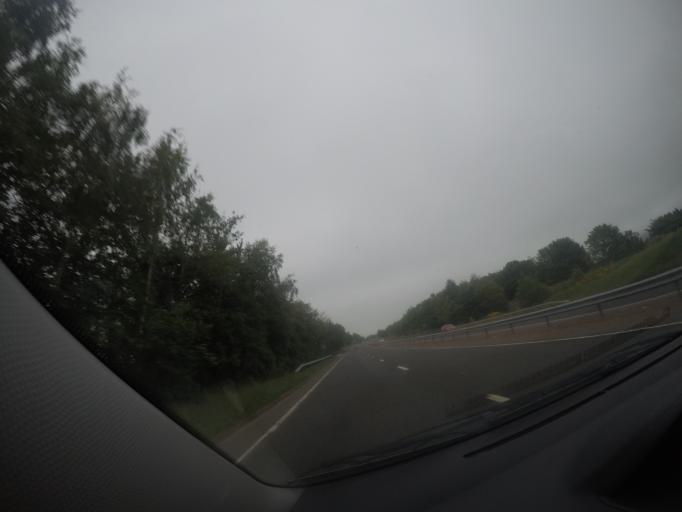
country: GB
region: Scotland
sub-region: Angus
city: Forfar
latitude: 56.5951
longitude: -2.9109
